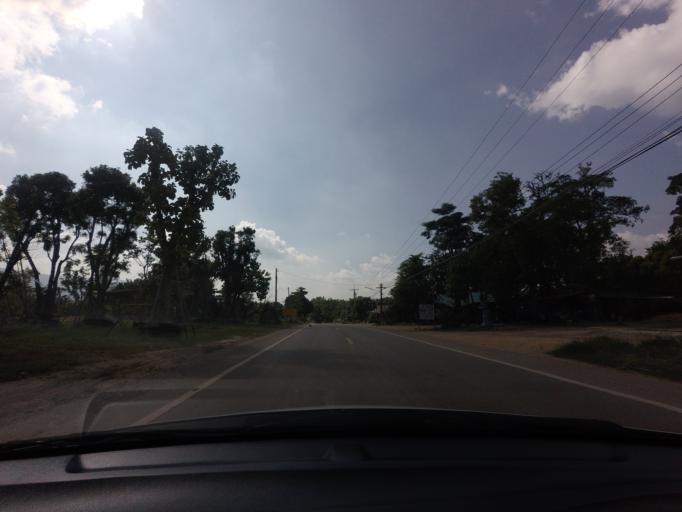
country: TH
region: Nakhon Ratchasima
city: Wang Nam Khiao
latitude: 14.4589
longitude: 101.6619
